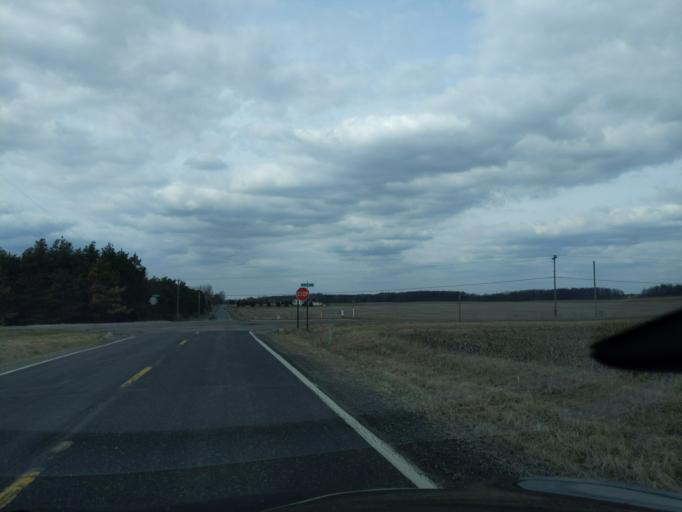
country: US
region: Michigan
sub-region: Ingham County
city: Mason
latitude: 42.5818
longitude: -84.4834
